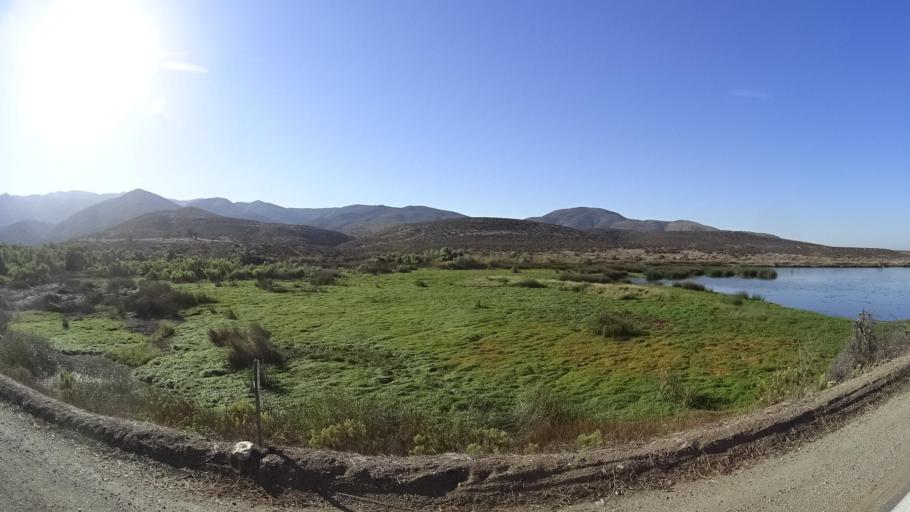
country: US
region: California
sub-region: San Diego County
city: Jamul
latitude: 32.6336
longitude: -116.9005
